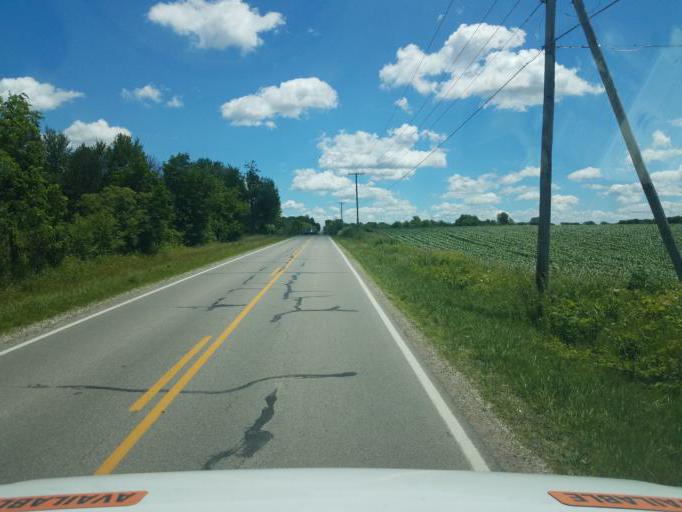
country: US
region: Ohio
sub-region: Crawford County
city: Galion
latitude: 40.7342
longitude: -82.8272
